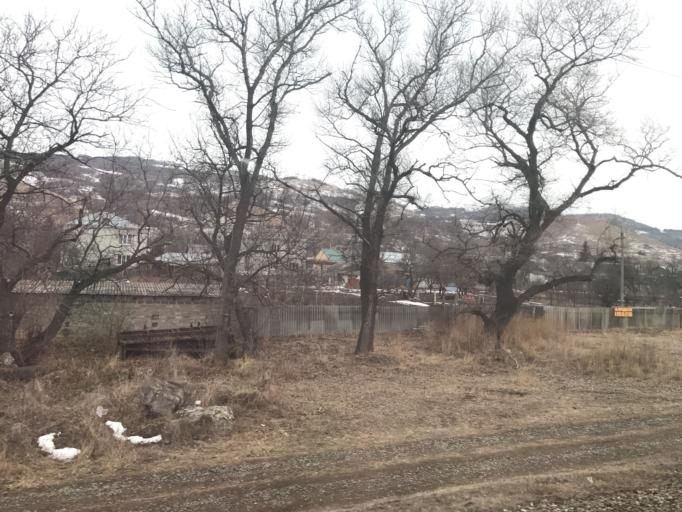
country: RU
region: Stavropol'skiy
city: Kislovodsk
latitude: 43.9556
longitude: 42.7598
